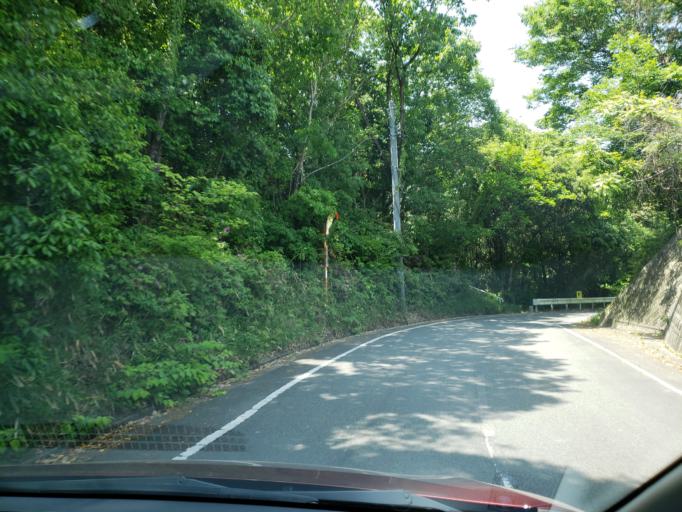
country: JP
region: Tokushima
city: Wakimachi
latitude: 34.0839
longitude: 134.2069
